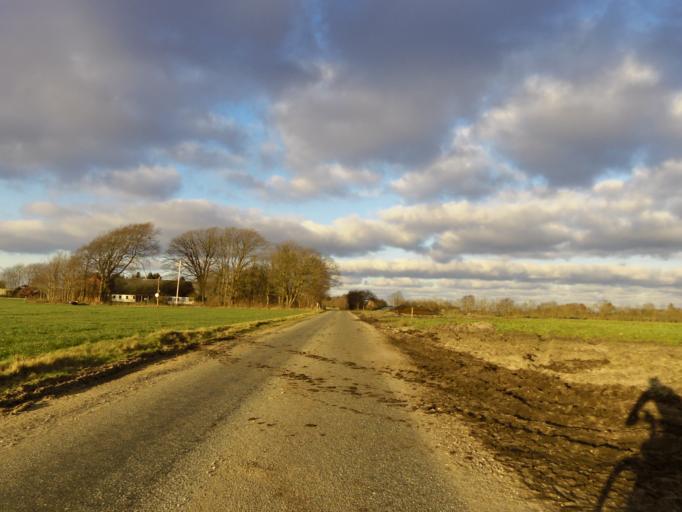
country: DK
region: South Denmark
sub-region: Esbjerg Kommune
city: Ribe
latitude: 55.2920
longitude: 8.8475
